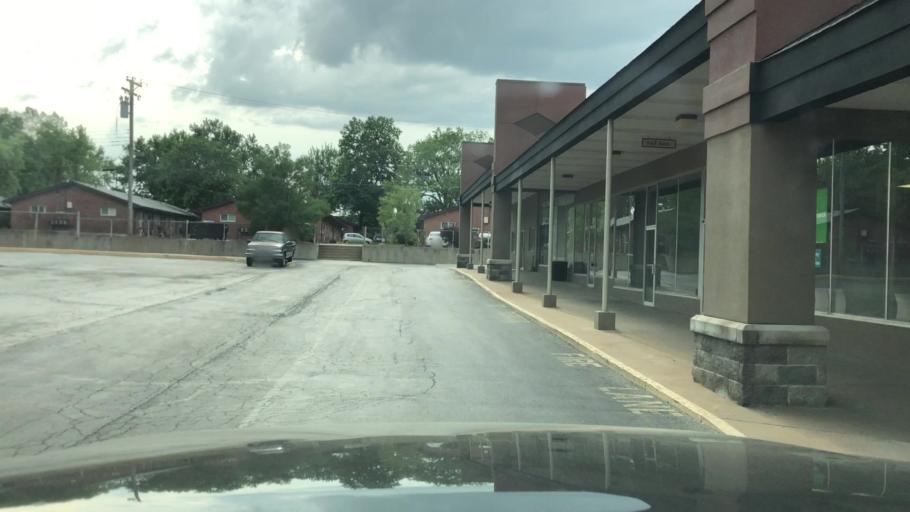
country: US
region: Missouri
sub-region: Saint Charles County
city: Saint Charles
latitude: 38.7850
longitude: -90.5123
